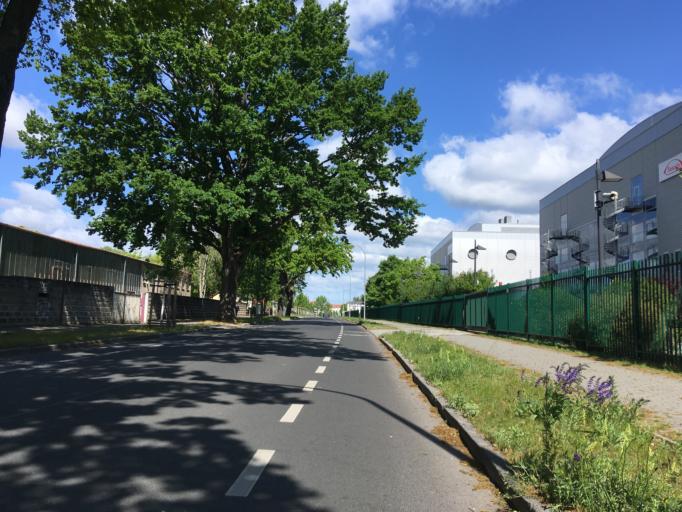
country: DE
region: Brandenburg
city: Oranienburg
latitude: 52.7474
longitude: 13.2528
